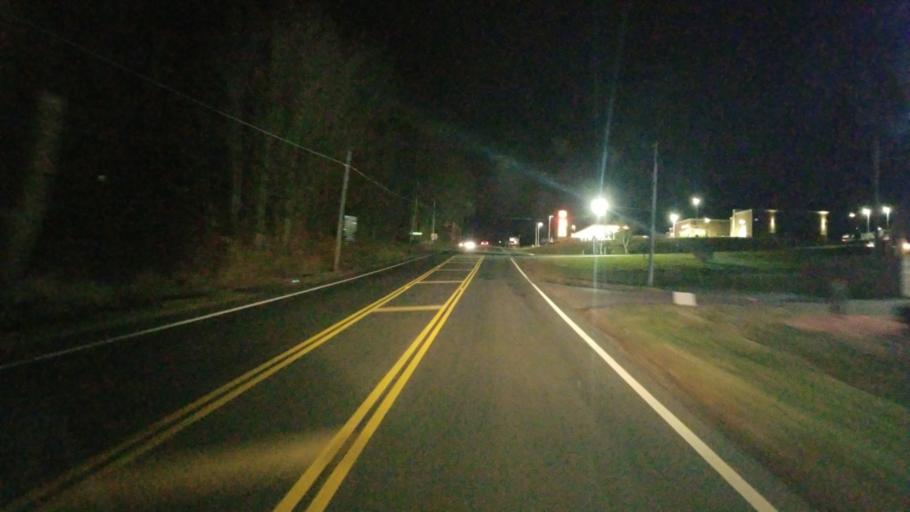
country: US
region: Ohio
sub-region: Knox County
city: Gambier
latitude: 40.4092
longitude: -82.3519
